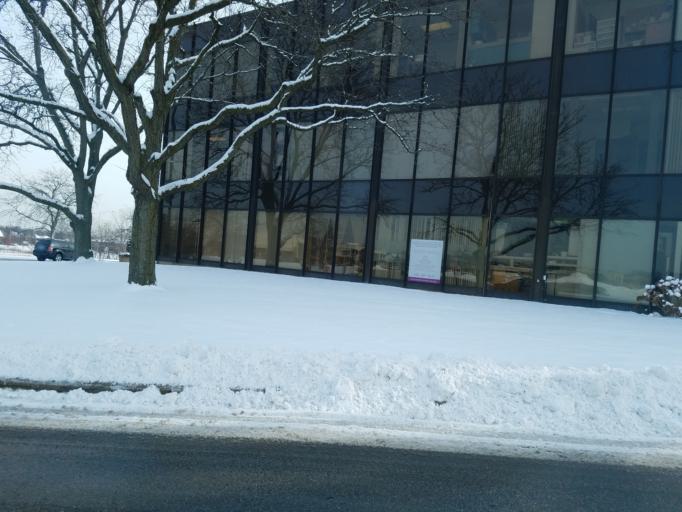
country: US
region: Illinois
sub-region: Cook County
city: Orland Park
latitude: 41.6171
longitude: -87.8442
